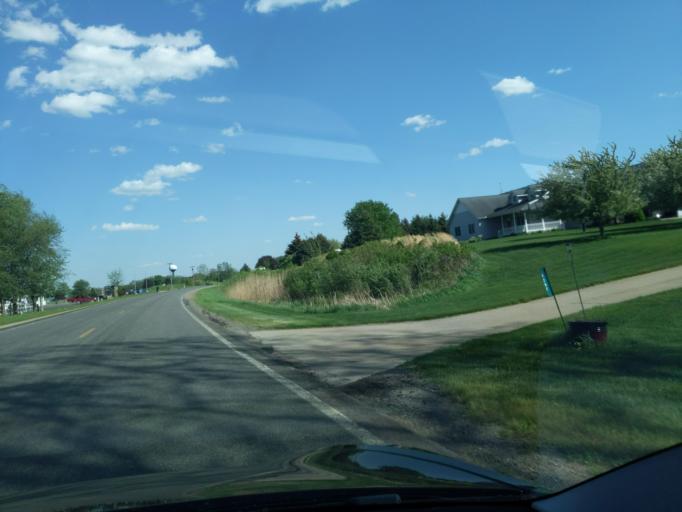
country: US
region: Michigan
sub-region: Ionia County
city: Lake Odessa
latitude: 42.7837
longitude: -85.1593
